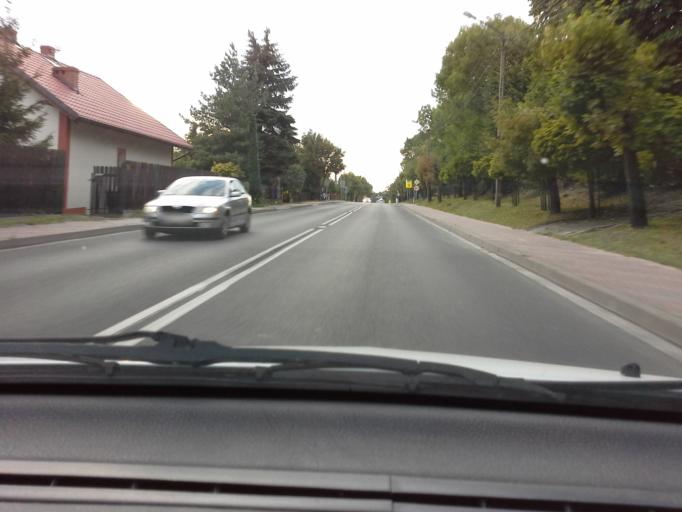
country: PL
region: Lesser Poland Voivodeship
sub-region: Powiat chrzanowski
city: Trzebinia
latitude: 50.1566
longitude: 19.4789
